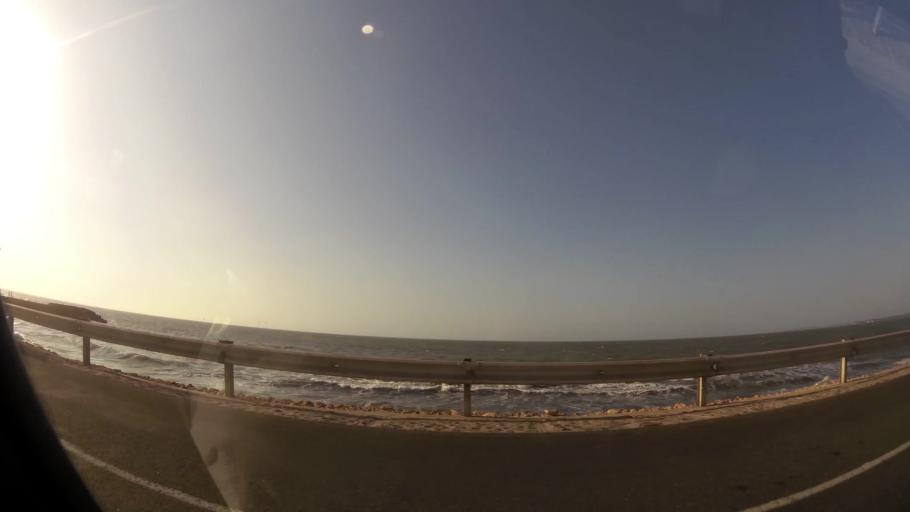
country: CO
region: Bolivar
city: Cartagena
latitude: 10.4511
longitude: -75.5175
